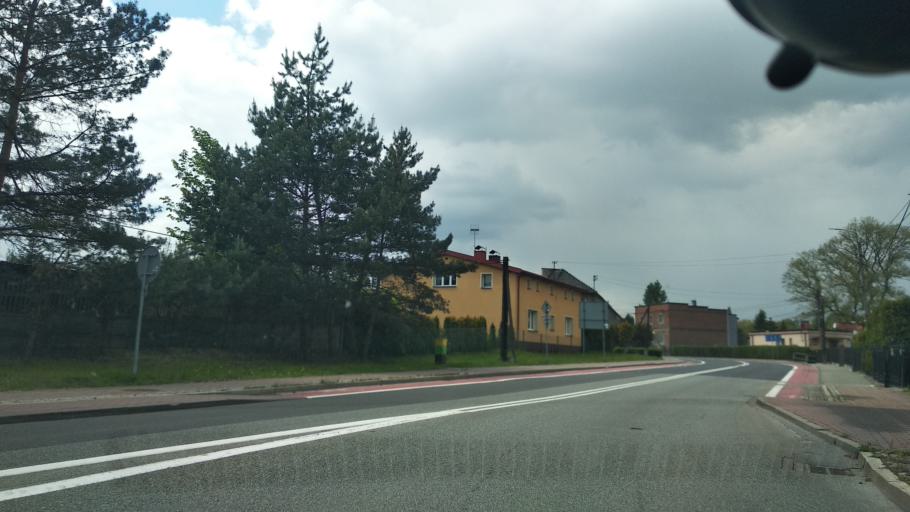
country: PL
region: Silesian Voivodeship
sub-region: Powiat mikolowski
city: Mikolow
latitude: 50.2282
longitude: 18.9226
